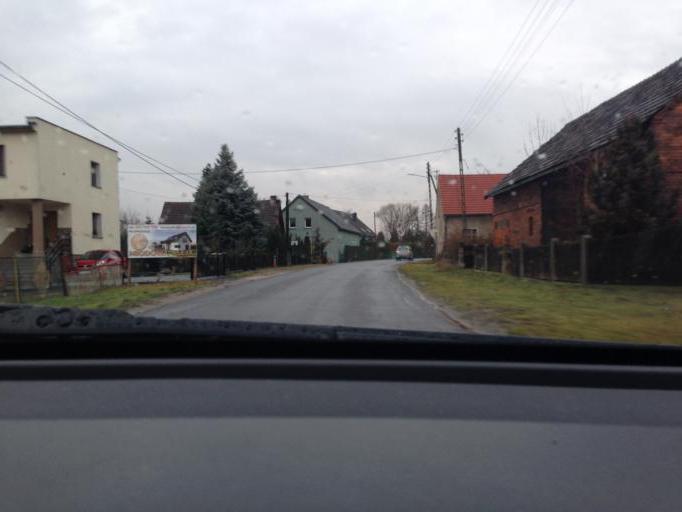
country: PL
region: Opole Voivodeship
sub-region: Powiat opolski
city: Wegry
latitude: 50.7261
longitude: 18.0710
